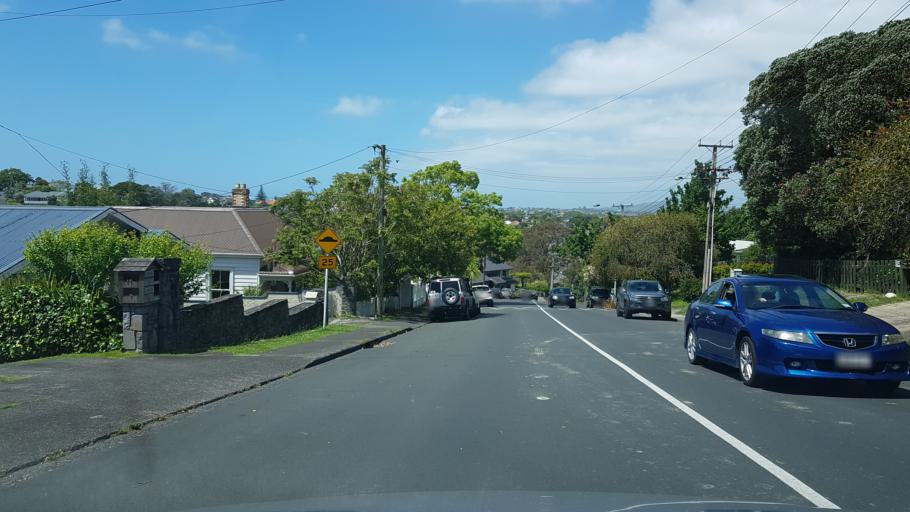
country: NZ
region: Auckland
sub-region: Auckland
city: North Shore
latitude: -36.8170
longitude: 174.7369
